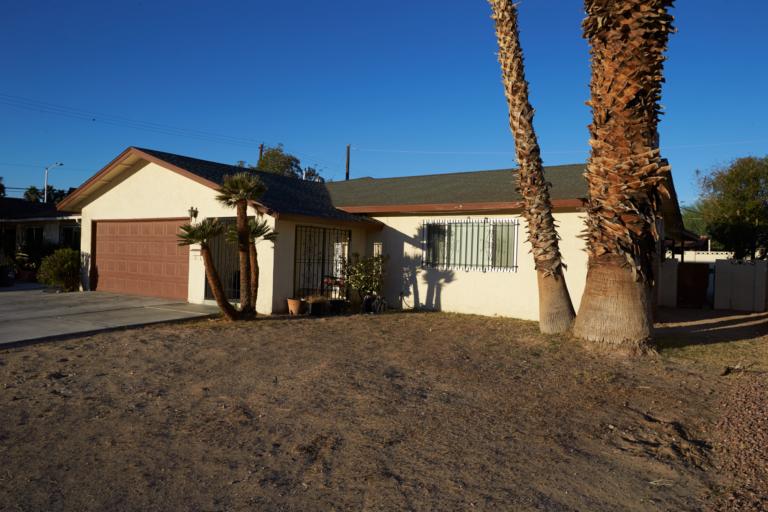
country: US
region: Nevada
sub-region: Clark County
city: Winchester
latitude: 36.1467
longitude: -115.1199
